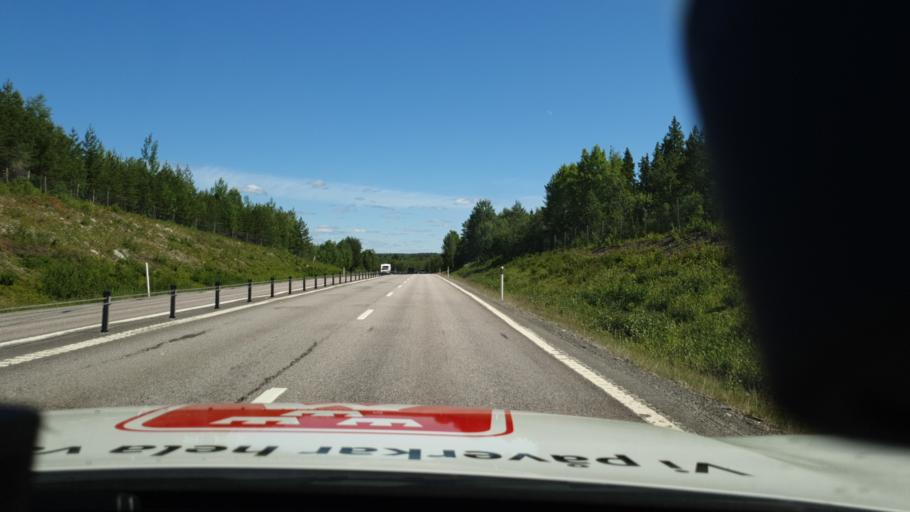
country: SE
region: Norrbotten
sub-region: Lulea Kommun
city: Ranea
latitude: 65.8719
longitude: 22.4558
